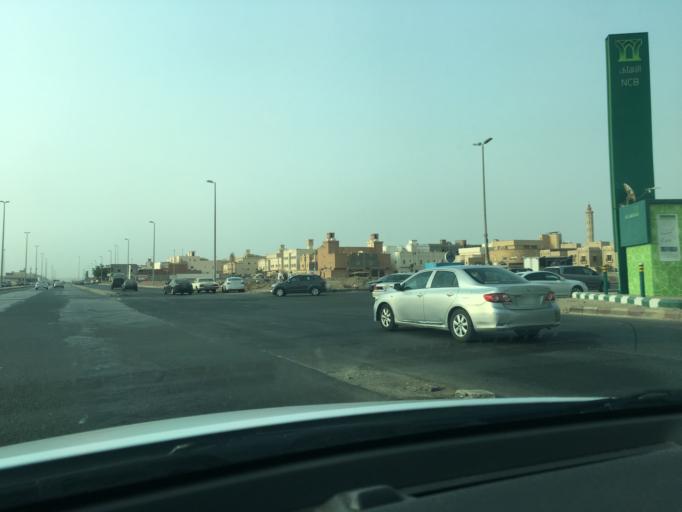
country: SA
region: Makkah
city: Jeddah
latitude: 21.7567
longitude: 39.1855
